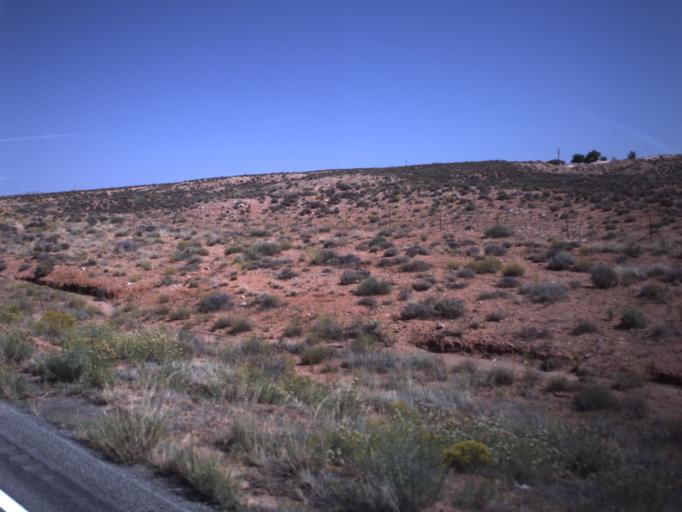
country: US
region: Utah
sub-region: San Juan County
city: Blanding
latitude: 37.0122
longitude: -109.6124
